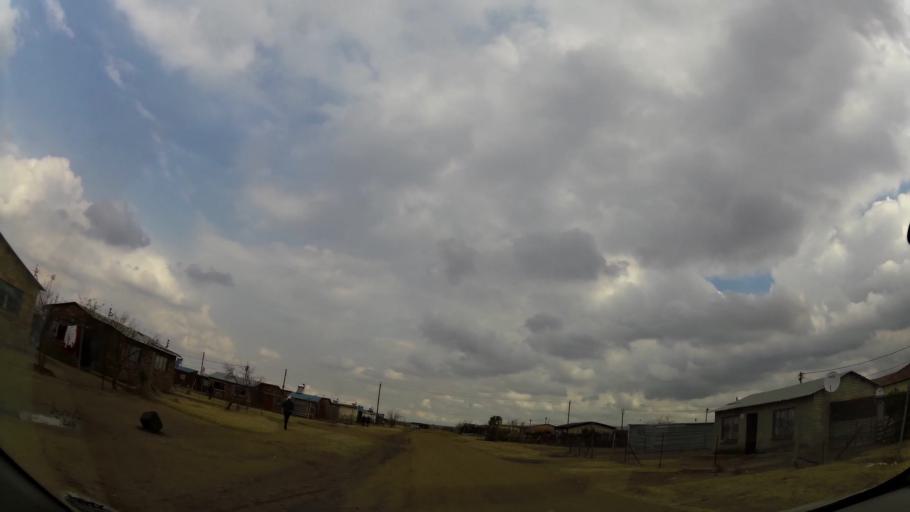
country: ZA
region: Orange Free State
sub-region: Fezile Dabi District Municipality
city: Sasolburg
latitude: -26.8609
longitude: 27.8919
